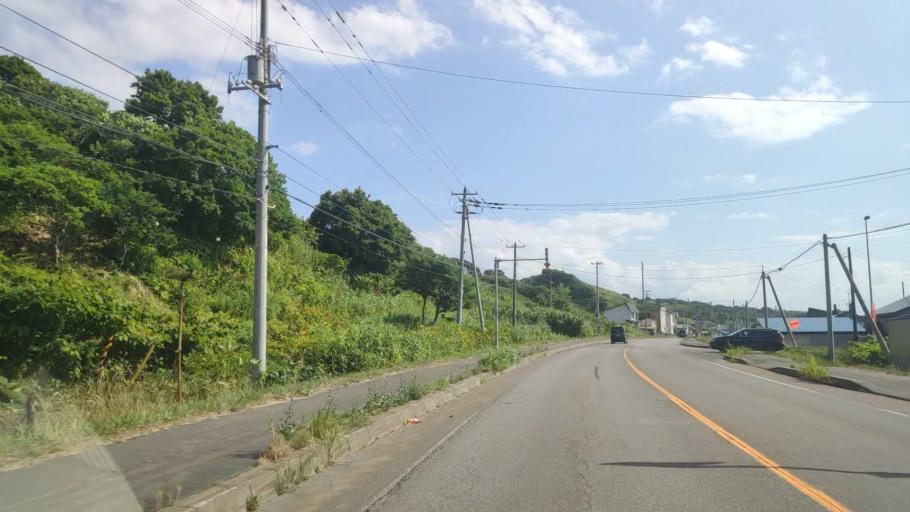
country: JP
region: Hokkaido
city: Rumoi
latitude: 43.9715
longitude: 141.6469
